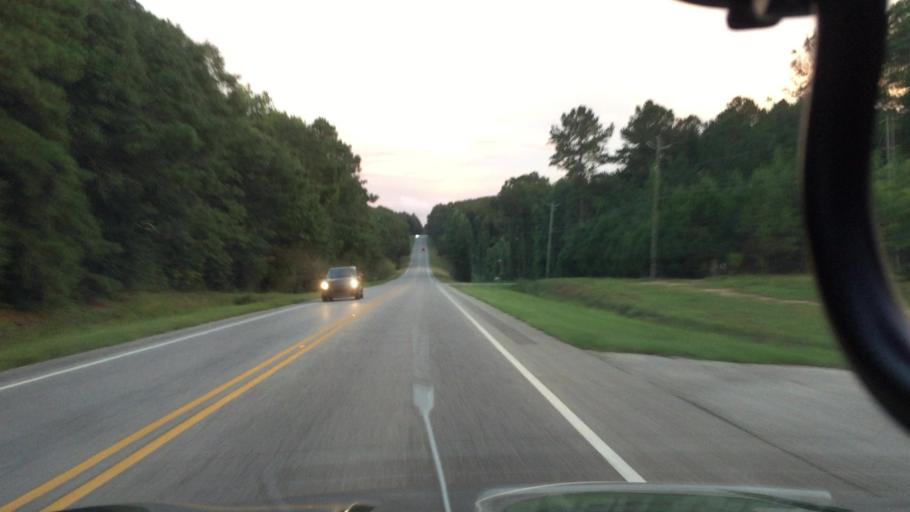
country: US
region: Alabama
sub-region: Coffee County
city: New Brockton
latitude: 31.3864
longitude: -85.8753
